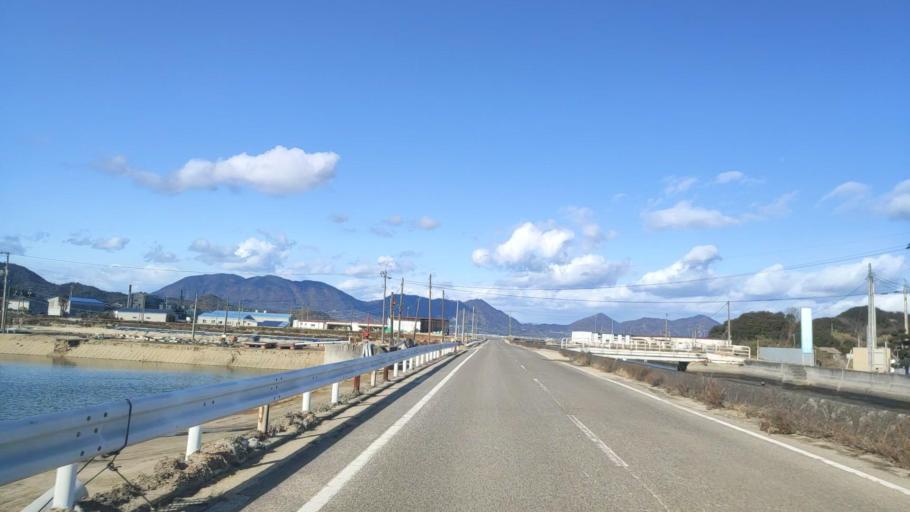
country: JP
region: Hiroshima
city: Innoshima
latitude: 34.2132
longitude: 133.1220
